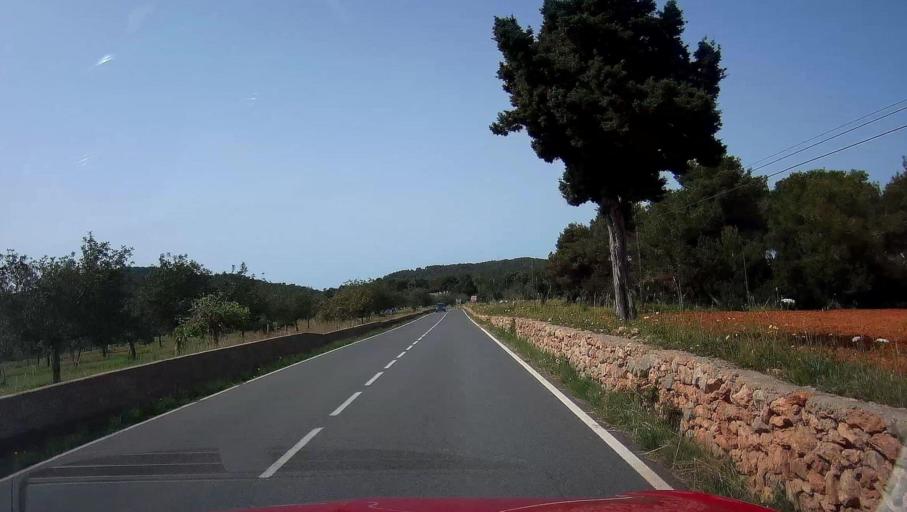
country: ES
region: Balearic Islands
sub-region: Illes Balears
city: Sant Joan de Labritja
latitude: 39.0510
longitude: 1.5730
